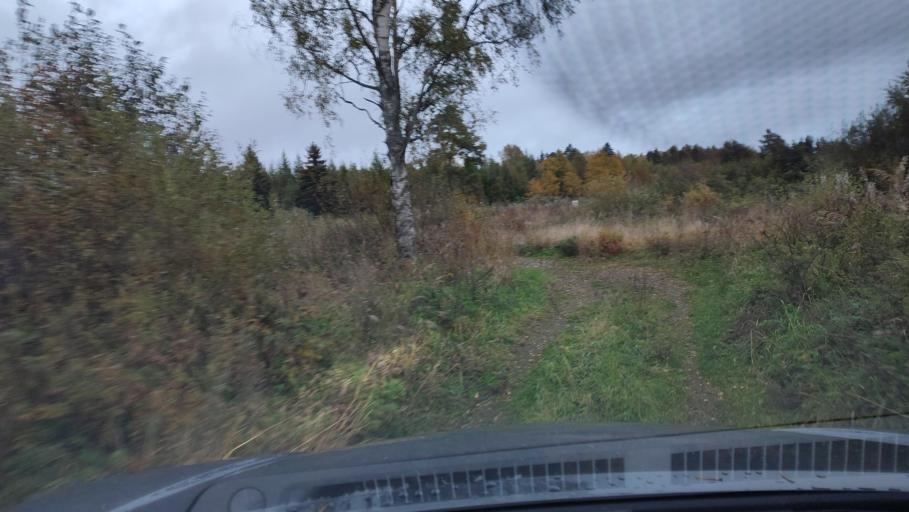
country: FI
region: Ostrobothnia
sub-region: Sydosterbotten
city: Kristinestad
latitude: 62.2781
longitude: 21.4079
